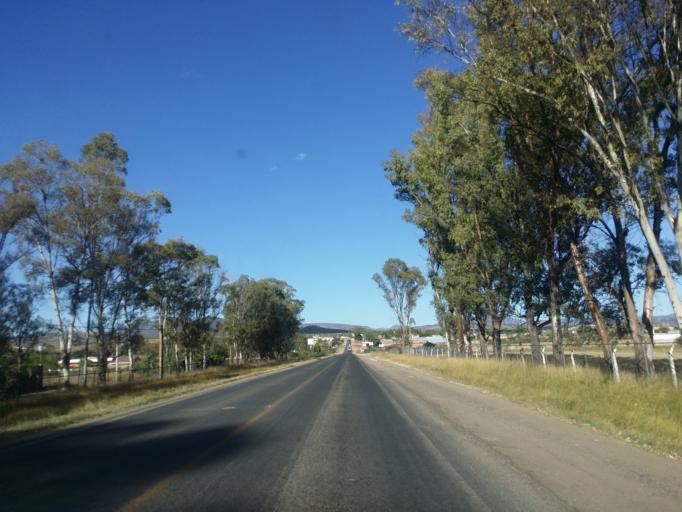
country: MX
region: Guanajuato
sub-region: Silao de la Victoria
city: El Refugio de los Sauces
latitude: 21.0349
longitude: -101.5259
